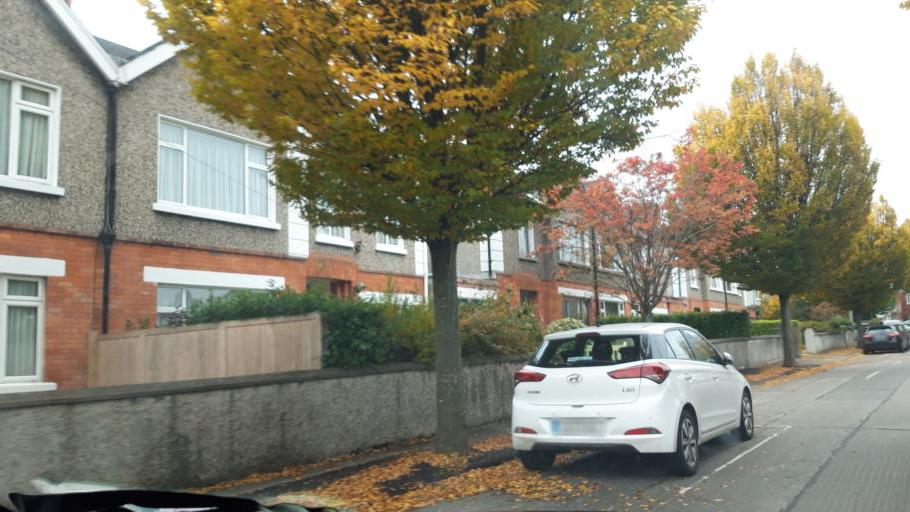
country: IE
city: Milltown
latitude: 53.3200
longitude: -6.2493
